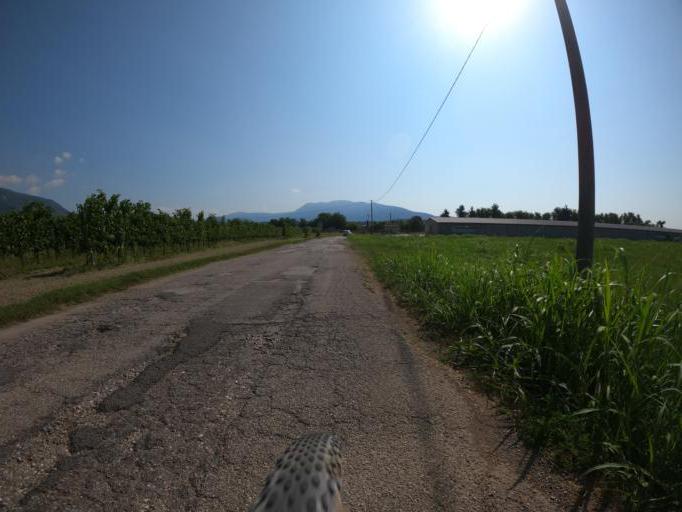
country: IT
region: Veneto
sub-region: Provincia di Verona
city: Costermano
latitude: 45.5874
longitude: 10.7607
